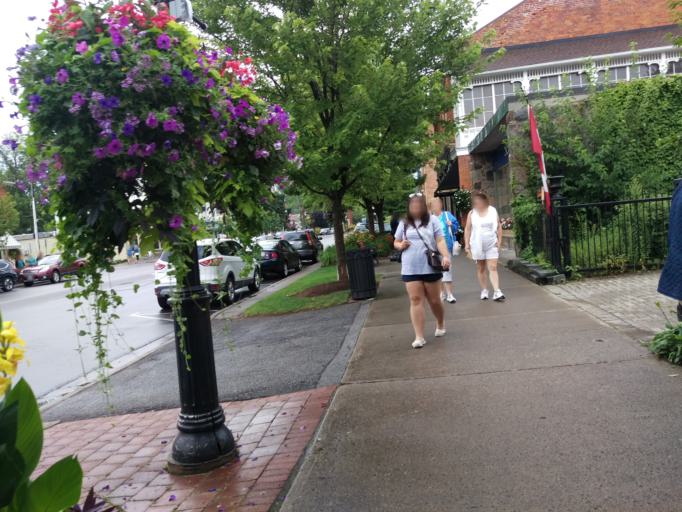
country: US
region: New York
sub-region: Niagara County
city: Youngstown
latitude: 43.2557
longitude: -79.0730
